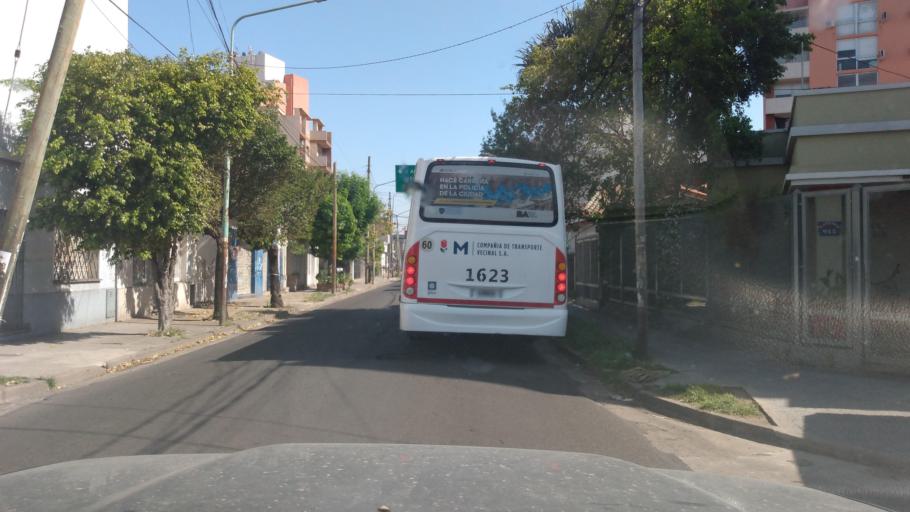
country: AR
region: Buenos Aires
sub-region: Partido de Moron
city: Moron
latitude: -34.6365
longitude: -58.5967
